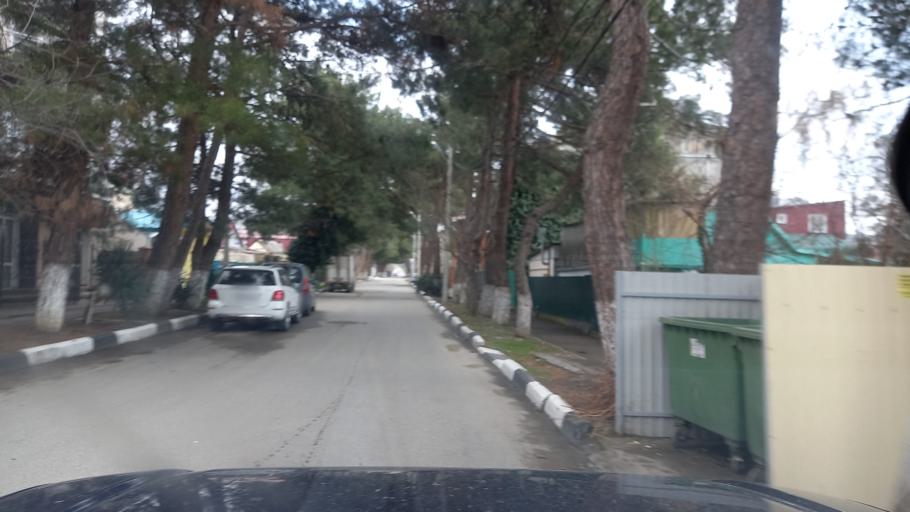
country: RU
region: Krasnodarskiy
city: Gelendzhik
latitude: 44.5601
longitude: 38.0859
